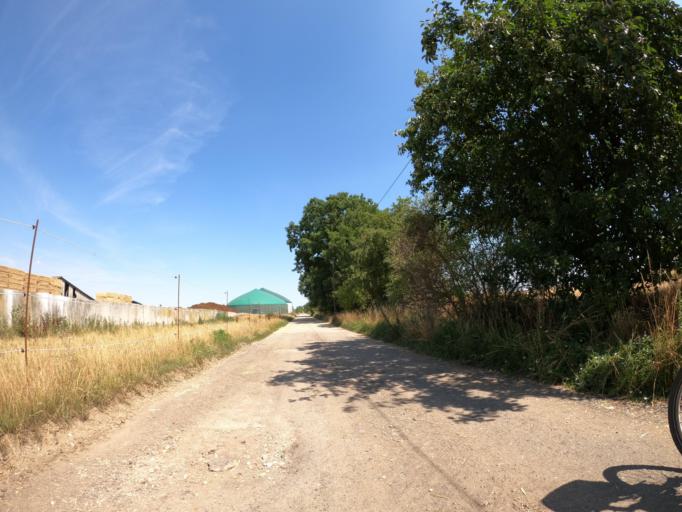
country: DE
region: Brandenburg
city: Mittenwalde
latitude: 53.2651
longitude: 13.5443
